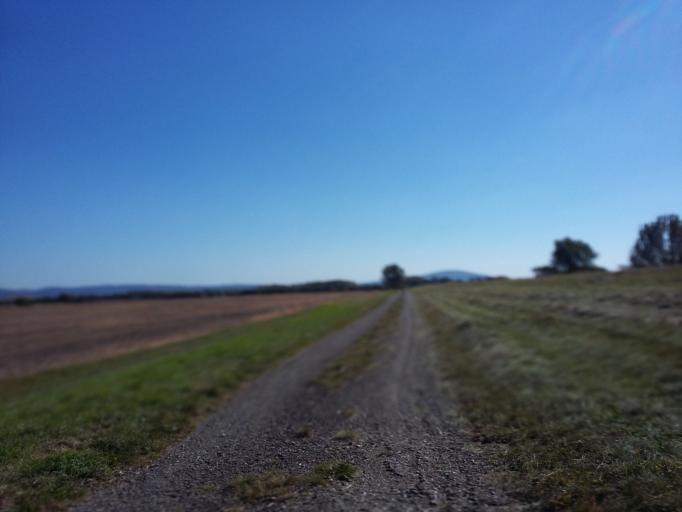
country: AT
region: Lower Austria
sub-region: Politischer Bezirk Ganserndorf
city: Marchegg
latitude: 48.3095
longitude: 16.9234
